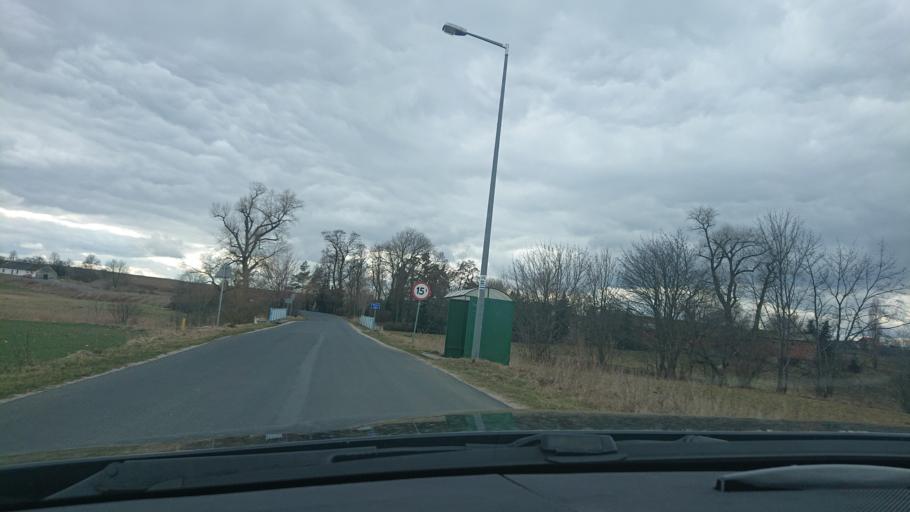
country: PL
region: Greater Poland Voivodeship
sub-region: Powiat gnieznienski
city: Gniezno
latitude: 52.5830
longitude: 17.6626
